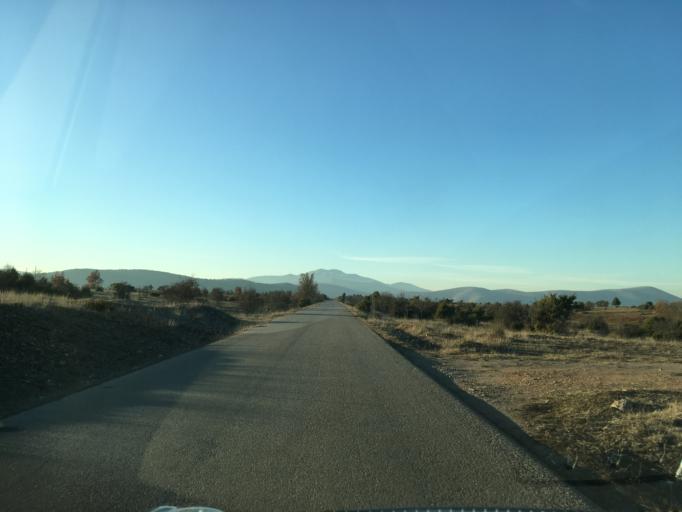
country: GR
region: West Macedonia
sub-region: Nomos Kozanis
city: Kozani
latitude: 40.2728
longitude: 21.7373
